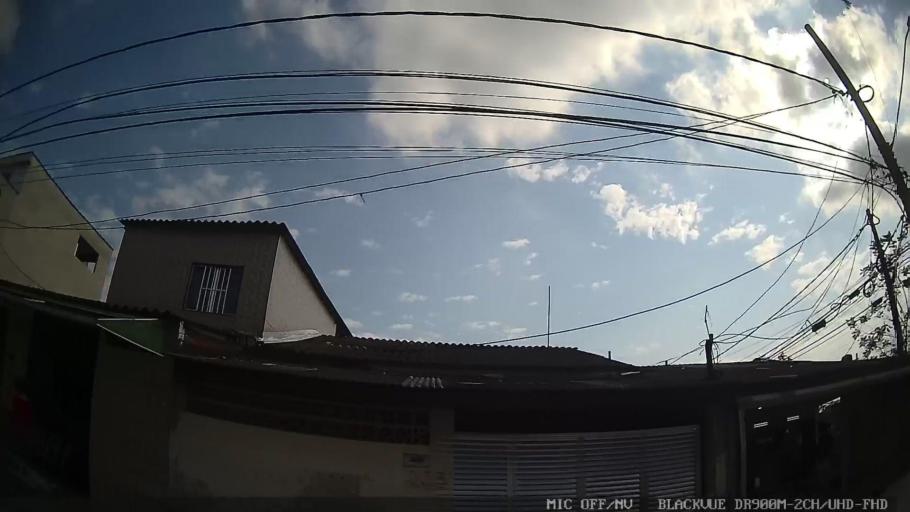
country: BR
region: Sao Paulo
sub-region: Santos
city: Santos
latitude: -23.9518
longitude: -46.2871
